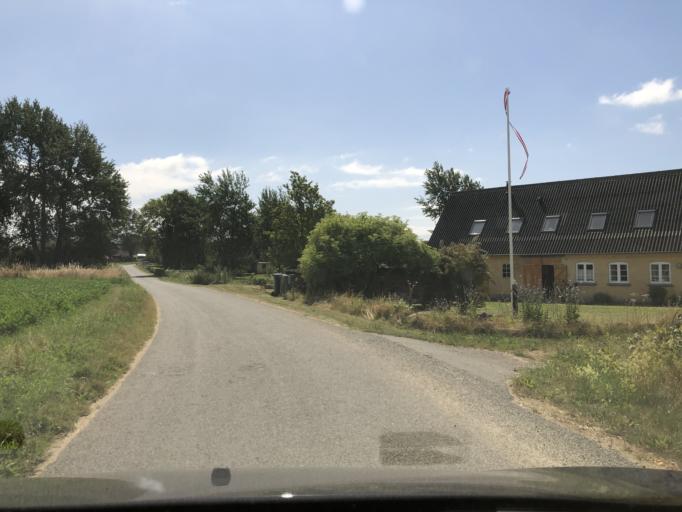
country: DK
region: South Denmark
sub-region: AEro Kommune
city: AEroskobing
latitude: 54.9324
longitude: 10.2820
